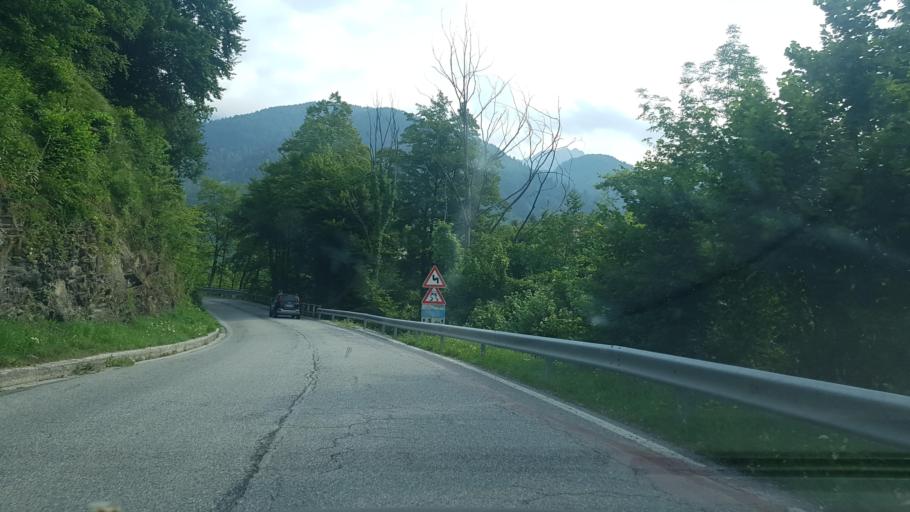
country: IT
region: Friuli Venezia Giulia
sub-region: Provincia di Udine
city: Paularo
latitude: 46.5082
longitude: 13.1205
